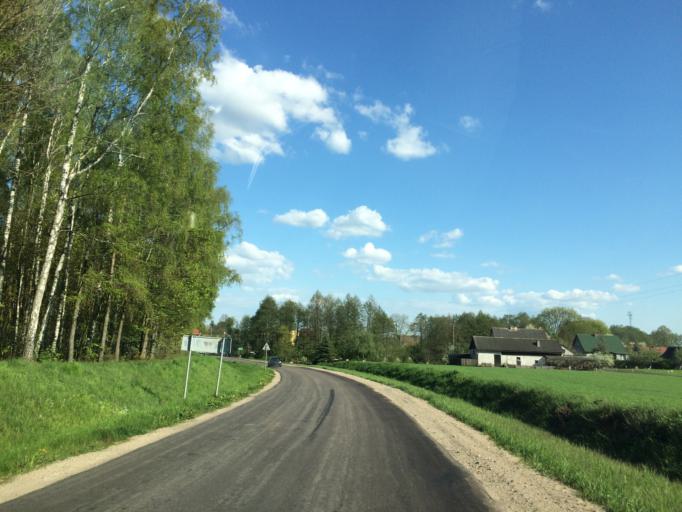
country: PL
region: Warmian-Masurian Voivodeship
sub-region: Powiat dzialdowski
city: Rybno
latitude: 53.3580
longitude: 19.9495
